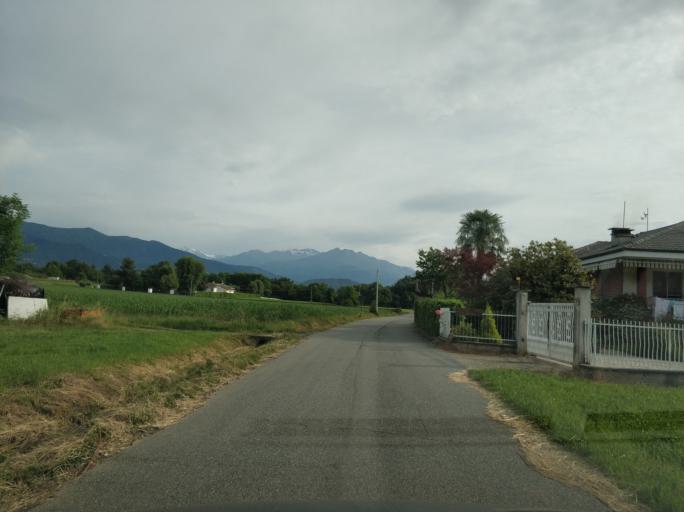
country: IT
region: Piedmont
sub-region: Provincia di Torino
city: Vauda Canavese Superiore
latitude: 45.2908
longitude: 7.6222
